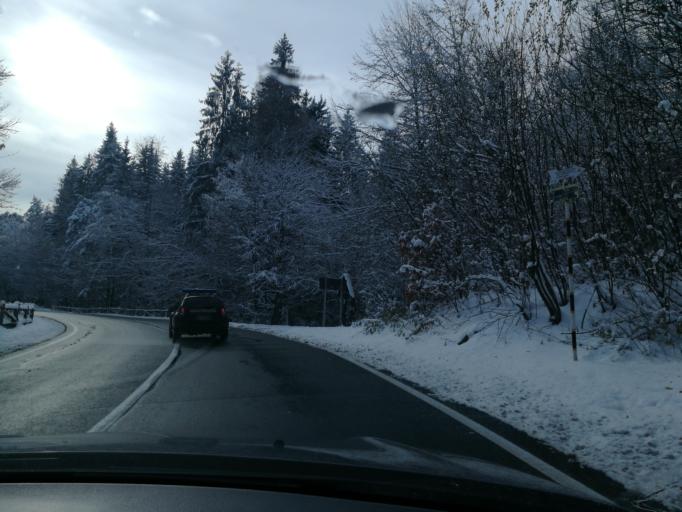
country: RO
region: Brasov
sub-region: Comuna Ghimbav
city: Ghimbav
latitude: 45.6202
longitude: 25.5428
